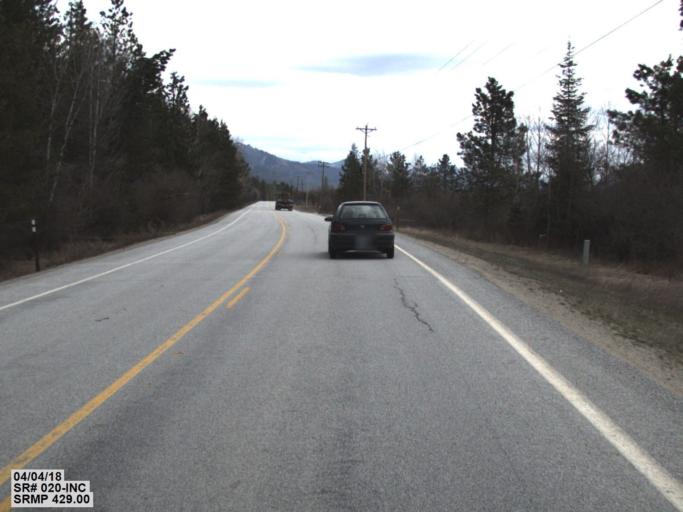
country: US
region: Washington
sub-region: Pend Oreille County
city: Newport
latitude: 48.2302
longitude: -117.1834
